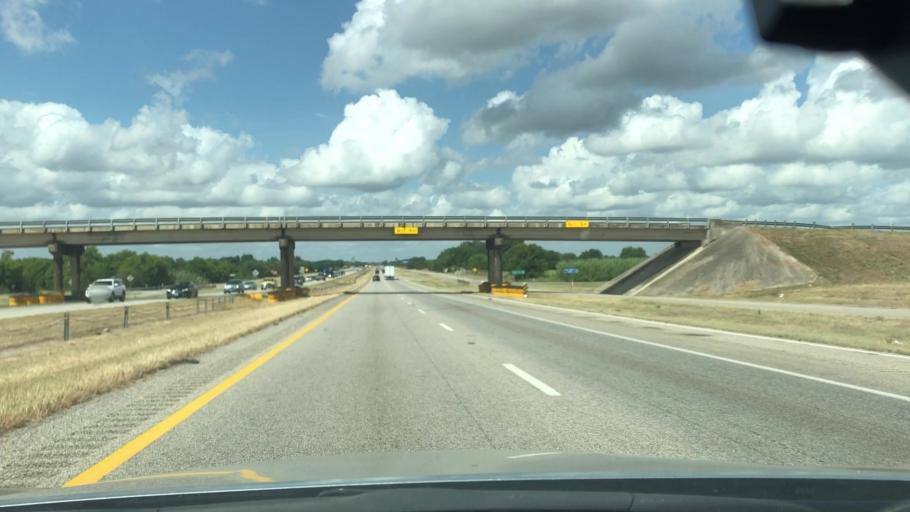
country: US
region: Texas
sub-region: Guadalupe County
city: Marion
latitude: 29.5084
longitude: -98.1674
